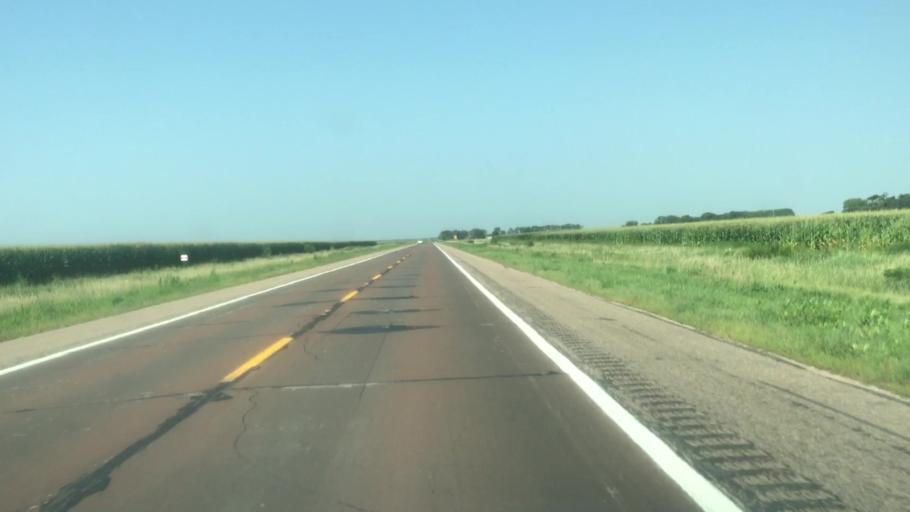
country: US
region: Nebraska
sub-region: Hall County
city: Grand Island
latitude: 40.9677
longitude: -98.4884
